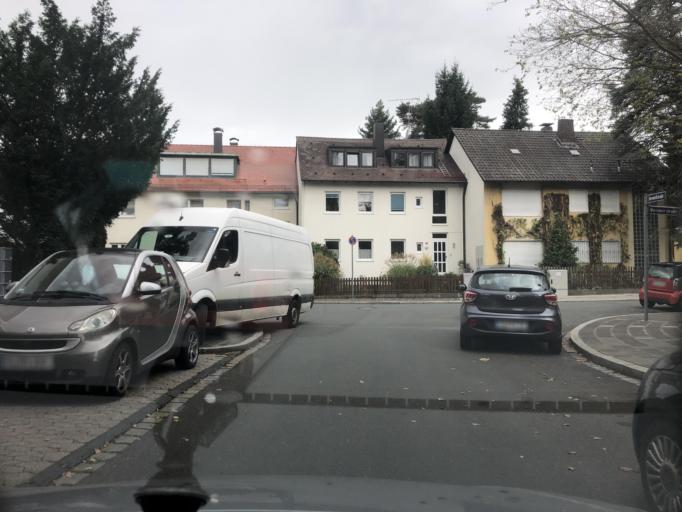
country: DE
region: Bavaria
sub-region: Regierungsbezirk Mittelfranken
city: Nuernberg
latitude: 49.4649
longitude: 11.0616
